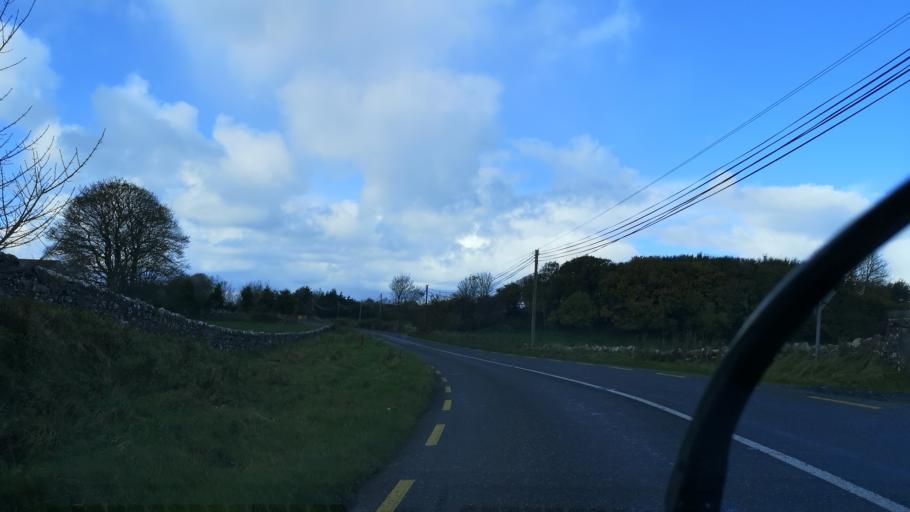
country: IE
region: Connaught
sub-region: Maigh Eo
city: Westport
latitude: 53.7783
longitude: -9.4183
